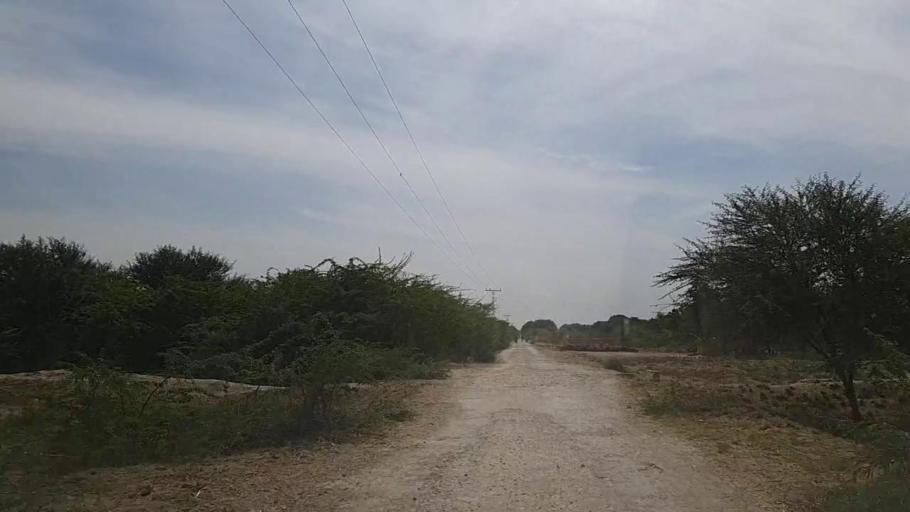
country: PK
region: Sindh
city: Samaro
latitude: 25.2598
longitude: 69.4535
